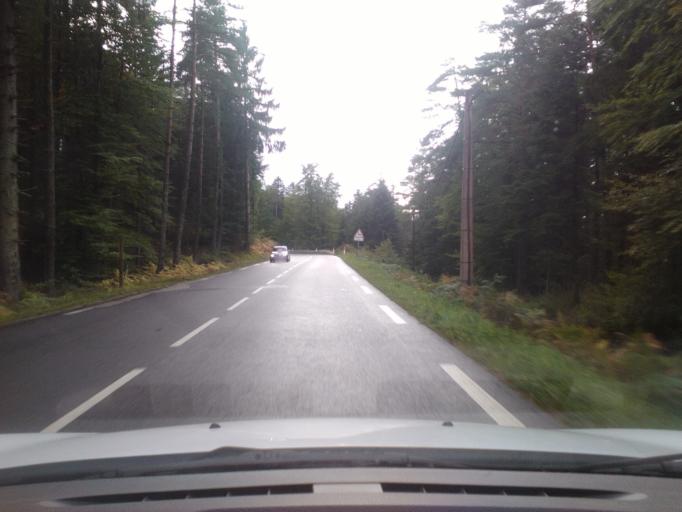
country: FR
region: Lorraine
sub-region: Departement des Vosges
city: Taintrux
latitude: 48.2743
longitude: 6.8612
